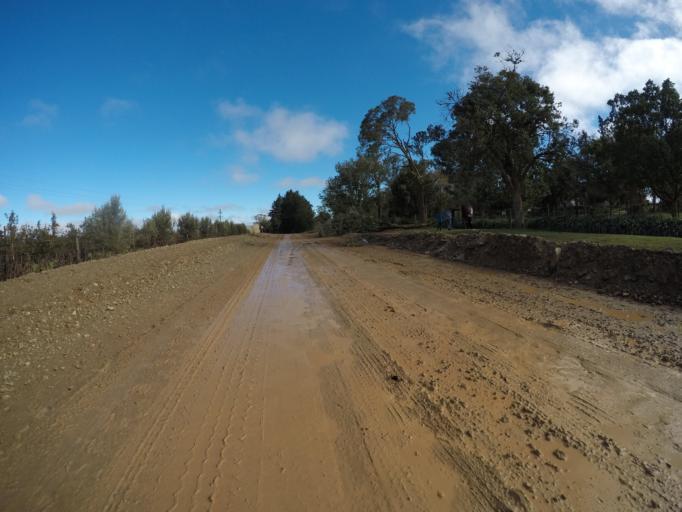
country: ZA
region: Western Cape
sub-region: Overberg District Municipality
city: Caledon
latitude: -34.1102
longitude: 19.7497
